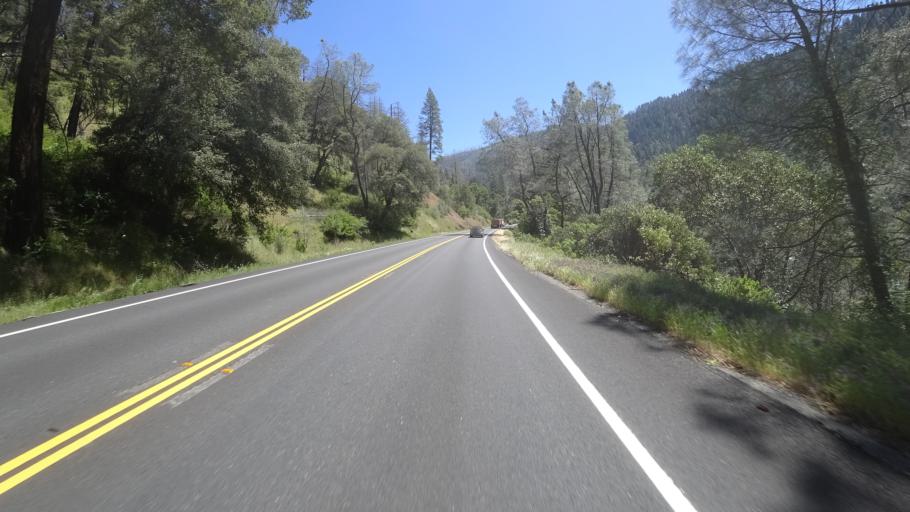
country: US
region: California
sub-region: Humboldt County
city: Willow Creek
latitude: 40.7876
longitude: -123.4285
